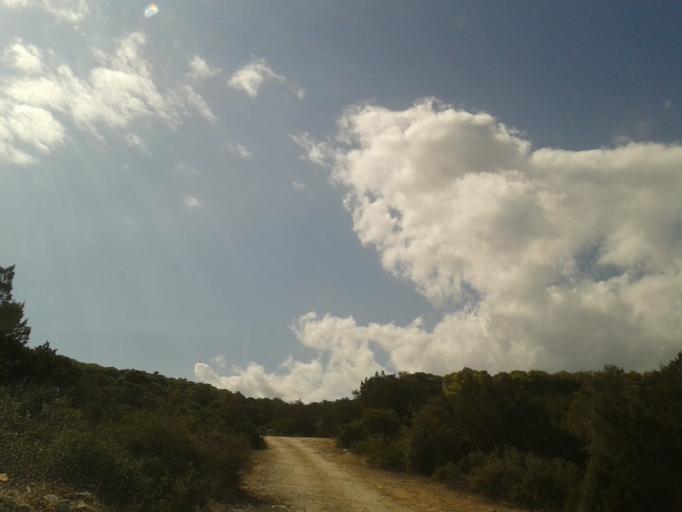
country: GR
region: Attica
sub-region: Nomarchia Anatolikis Attikis
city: Kato Soulion
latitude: 38.2256
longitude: 24.0233
